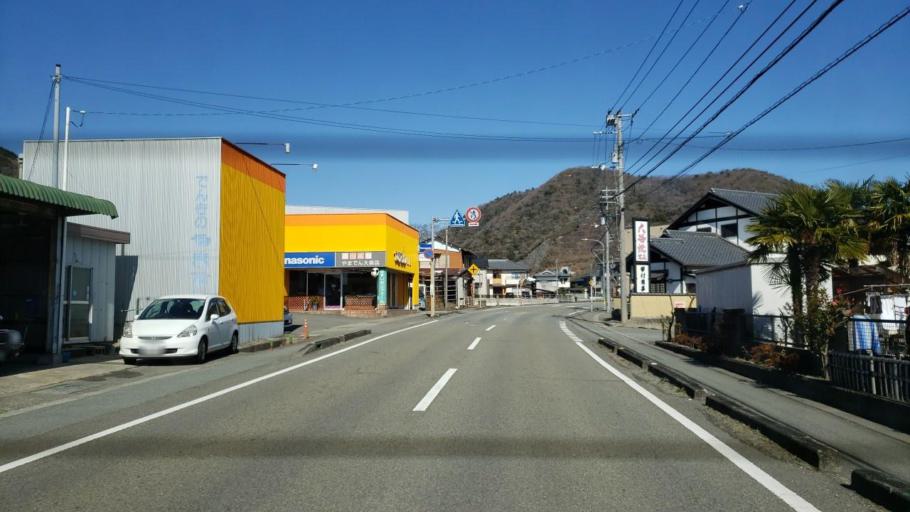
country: JP
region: Tokushima
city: Narutocho-mitsuishi
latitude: 34.1606
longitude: 134.5380
